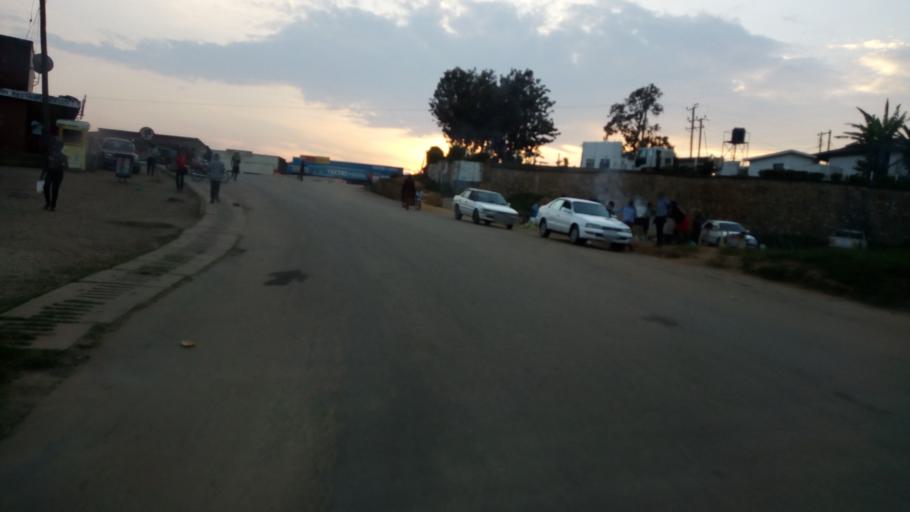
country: UG
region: Western Region
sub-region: Rukungiri District
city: Rukungiri
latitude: -0.7910
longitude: 29.9271
